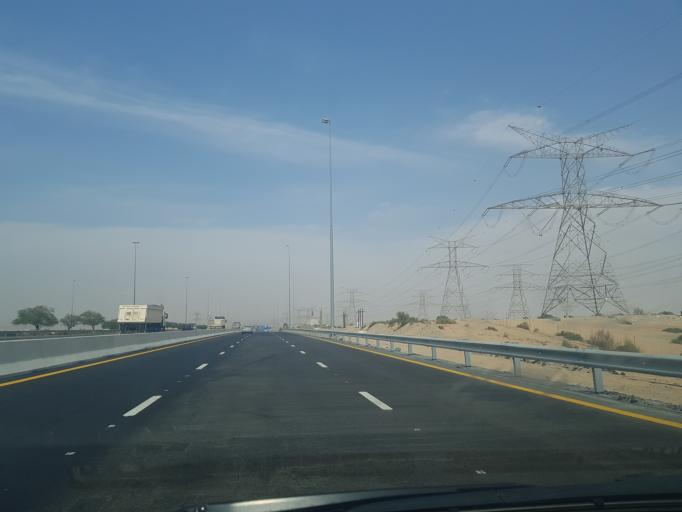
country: AE
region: Ash Shariqah
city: Sharjah
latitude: 25.2212
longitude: 55.5586
